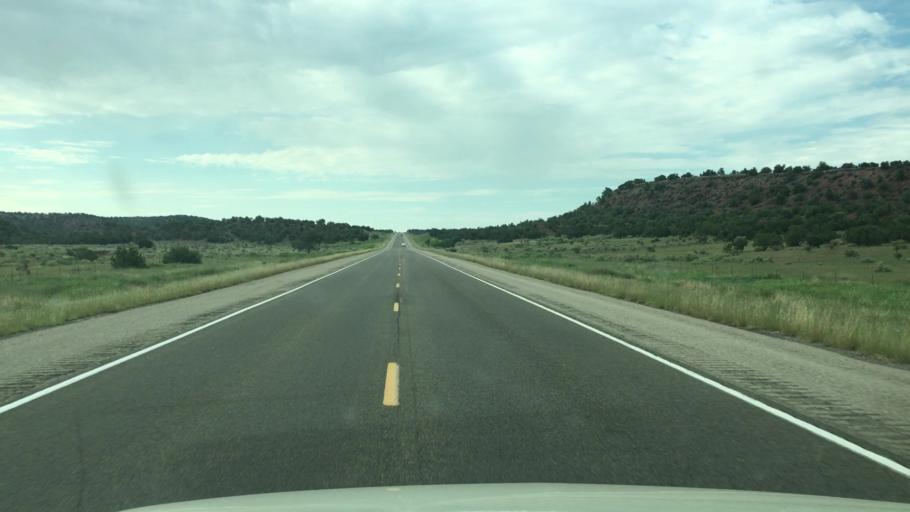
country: US
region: New Mexico
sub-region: Santa Fe County
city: Eldorado at Santa Fe
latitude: 35.2403
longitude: -105.8053
